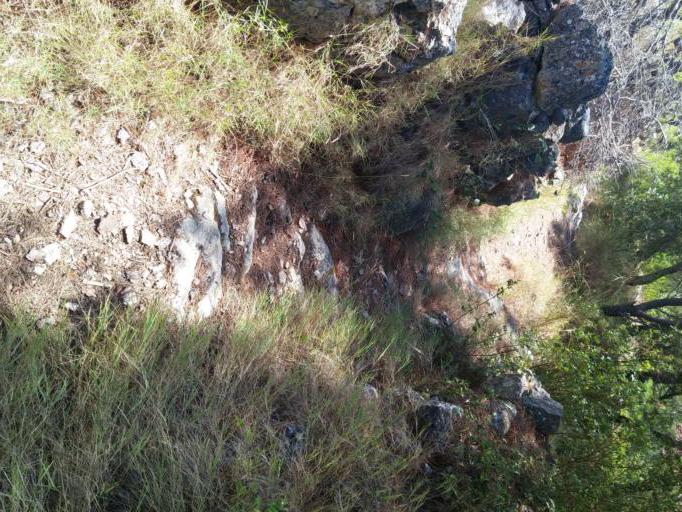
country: HR
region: Sibensko-Kniniska
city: Vodice
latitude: 43.7262
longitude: 15.7996
